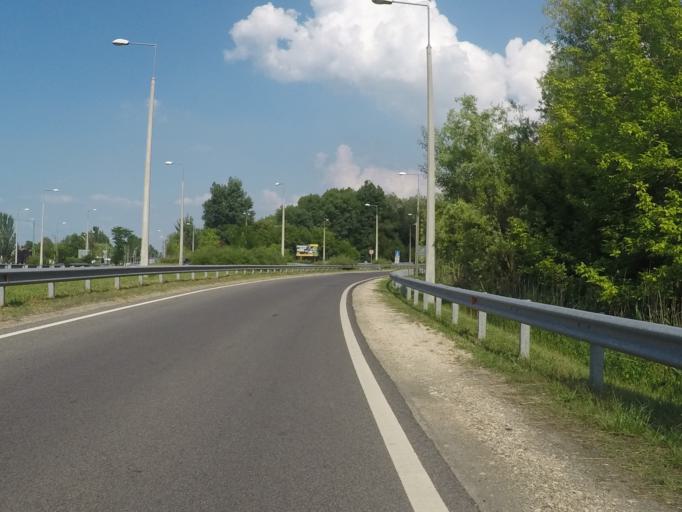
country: HU
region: Somogy
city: Zamardi
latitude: 46.8846
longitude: 17.9653
